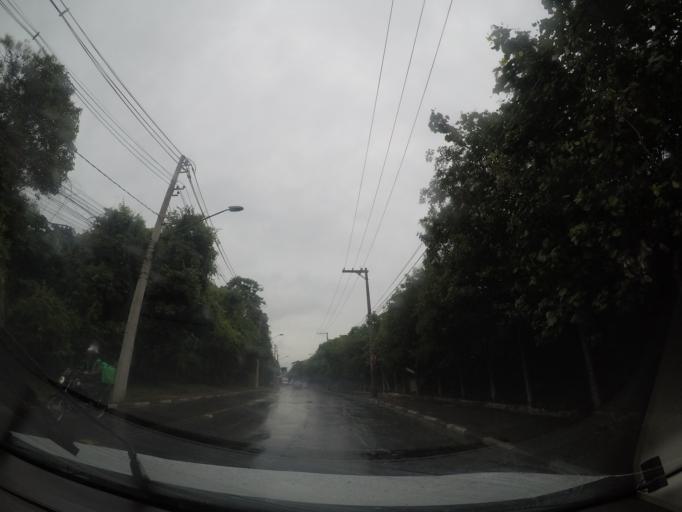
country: BR
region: Sao Paulo
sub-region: Guarulhos
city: Guarulhos
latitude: -23.4560
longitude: -46.4865
